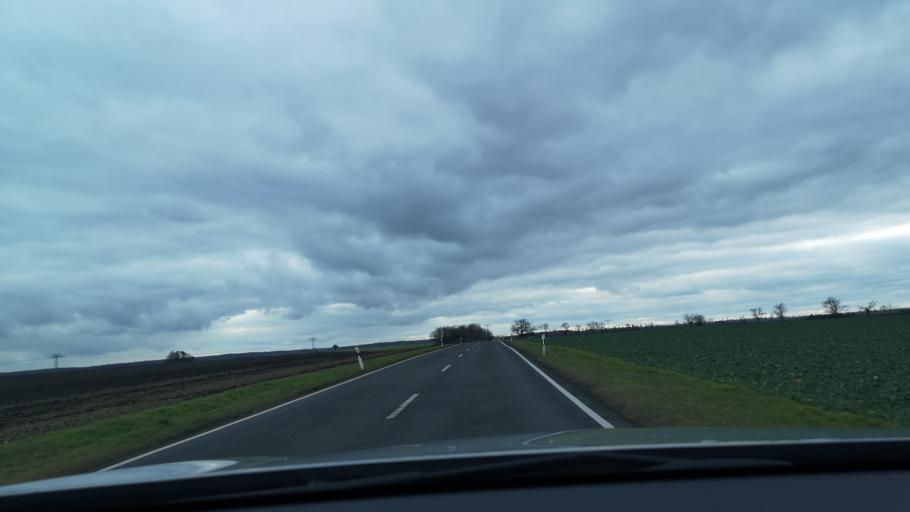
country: DE
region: Saxony-Anhalt
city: Mucheln
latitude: 51.2934
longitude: 11.7995
